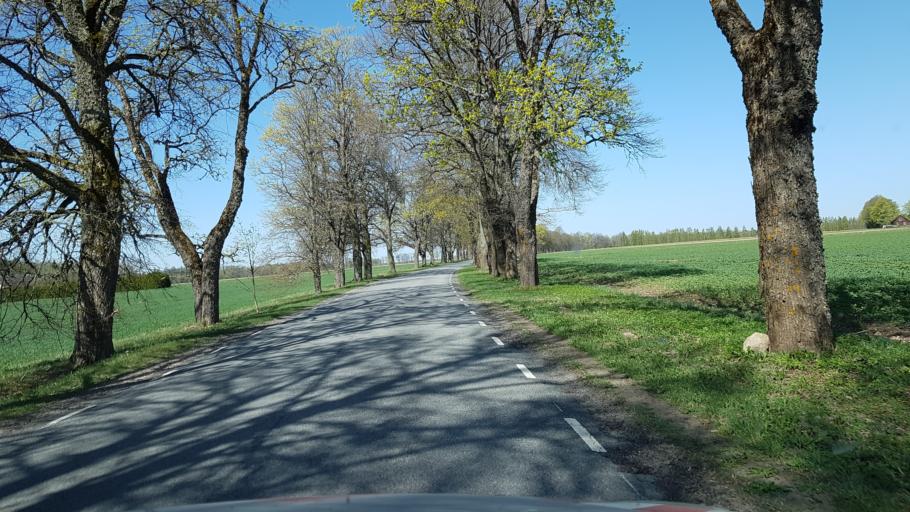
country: EE
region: Viljandimaa
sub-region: Vohma linn
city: Vohma
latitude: 58.5416
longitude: 25.5748
